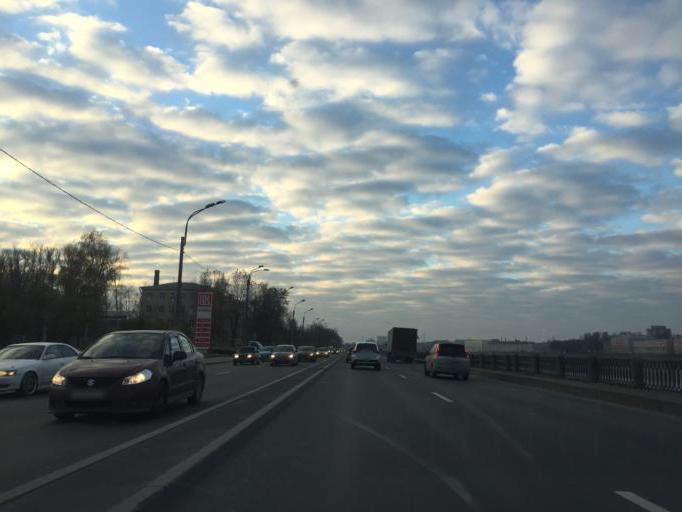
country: RU
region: St.-Petersburg
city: Obukhovo
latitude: 59.8918
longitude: 30.4473
